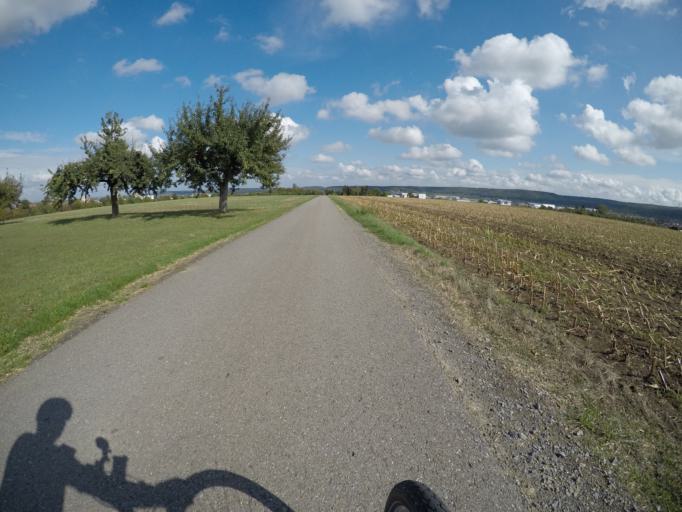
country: DE
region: Baden-Wuerttemberg
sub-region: Regierungsbezirk Stuttgart
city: Nufringen
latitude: 48.6341
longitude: 8.8862
